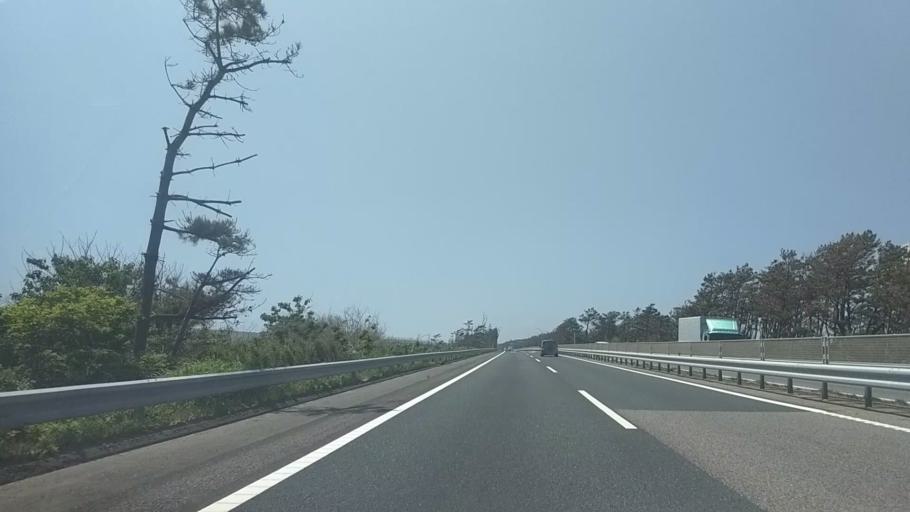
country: JP
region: Shizuoka
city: Hamamatsu
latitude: 34.6767
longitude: 137.6328
